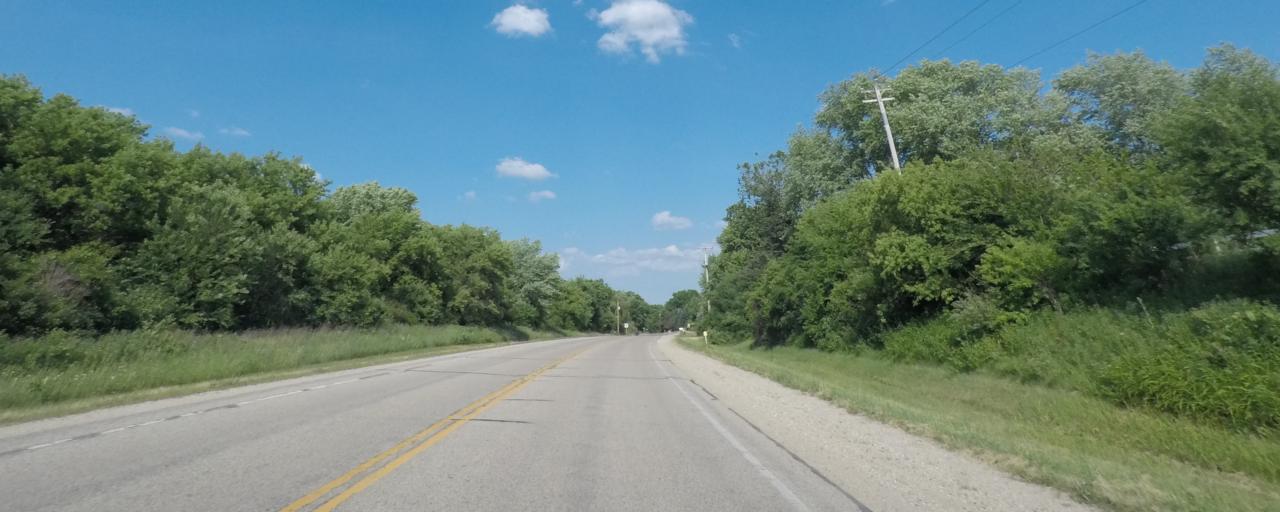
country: US
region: Wisconsin
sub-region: Walworth County
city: Potter Lake
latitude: 42.8282
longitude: -88.3105
